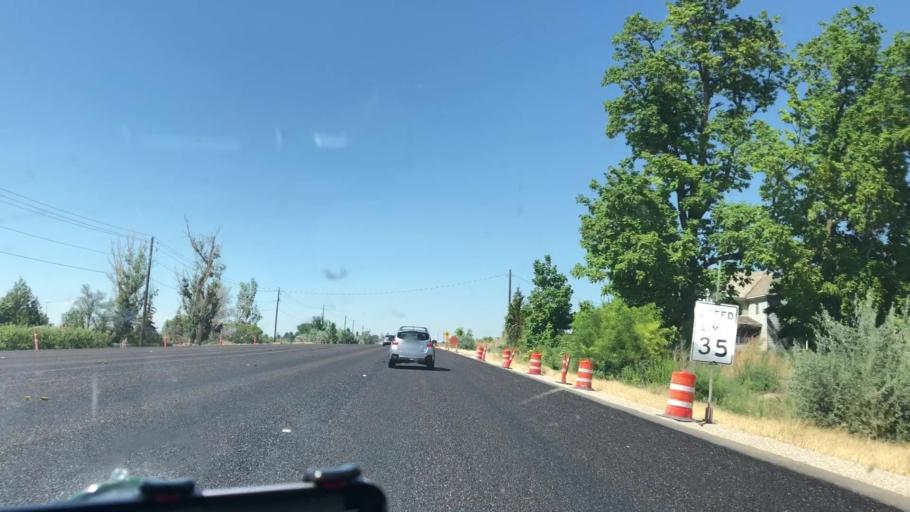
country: US
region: Idaho
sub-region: Owyhee County
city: Marsing
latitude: 43.5919
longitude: -116.7923
